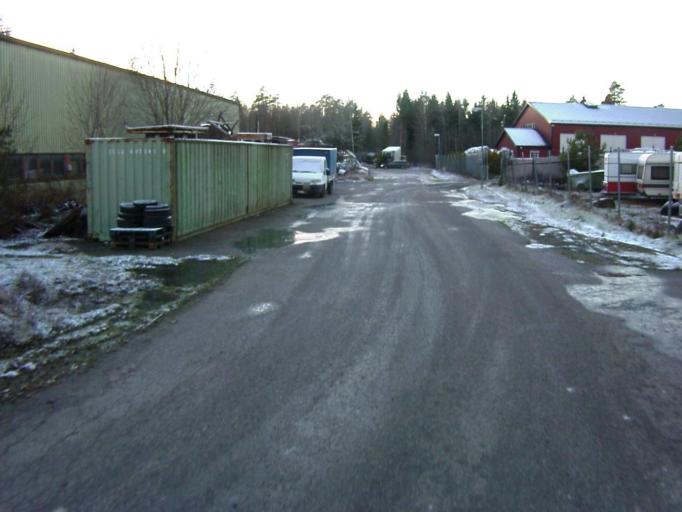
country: SE
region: Soedermanland
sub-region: Eskilstuna Kommun
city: Arla
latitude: 59.3198
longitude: 16.5919
